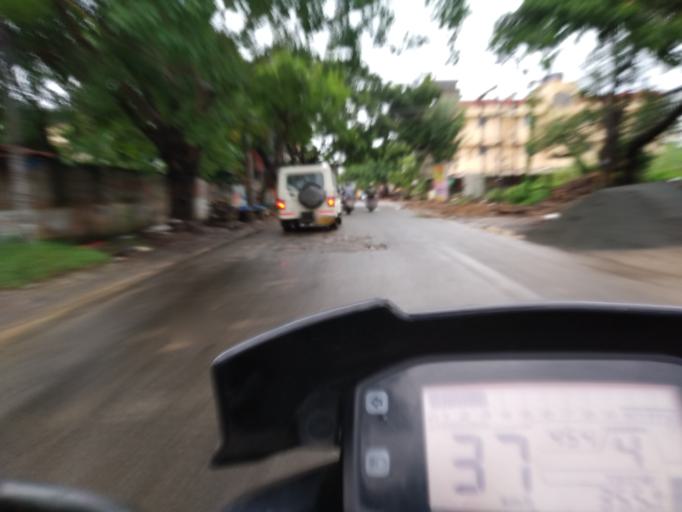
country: IN
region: Kerala
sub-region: Ernakulam
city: Cochin
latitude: 9.9733
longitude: 76.3087
